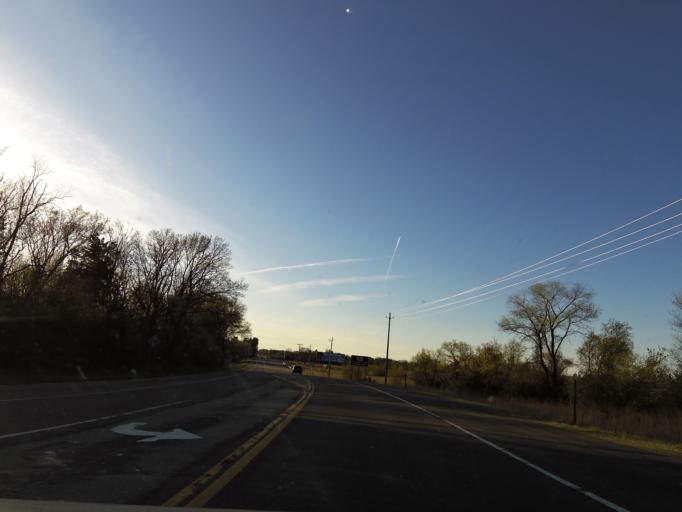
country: US
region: Wisconsin
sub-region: Pierce County
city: Prescott
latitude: 44.6562
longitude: -92.7684
